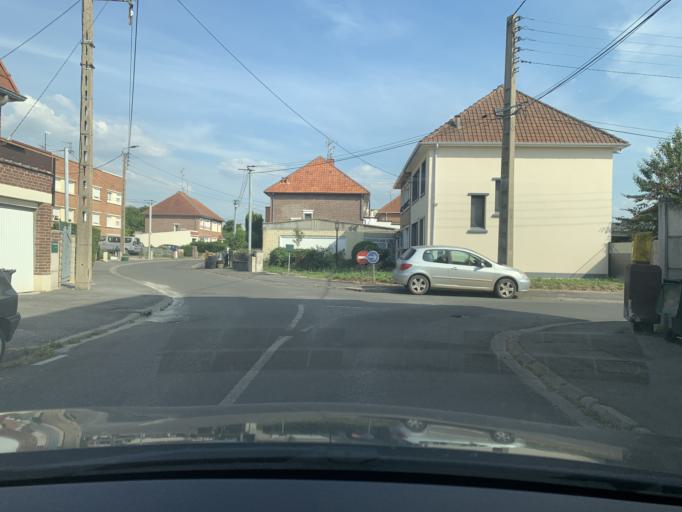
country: FR
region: Nord-Pas-de-Calais
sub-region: Departement du Nord
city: Cambrai
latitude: 50.1670
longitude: 3.2511
